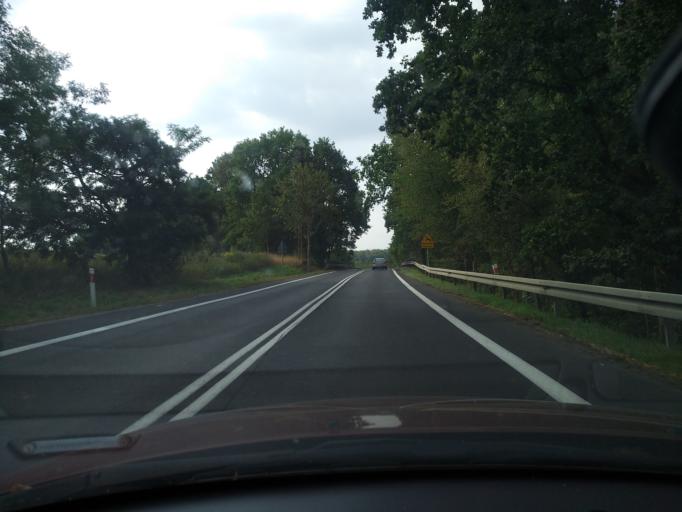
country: PL
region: Lower Silesian Voivodeship
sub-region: Powiat lubanski
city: Luban
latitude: 51.0886
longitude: 15.3223
